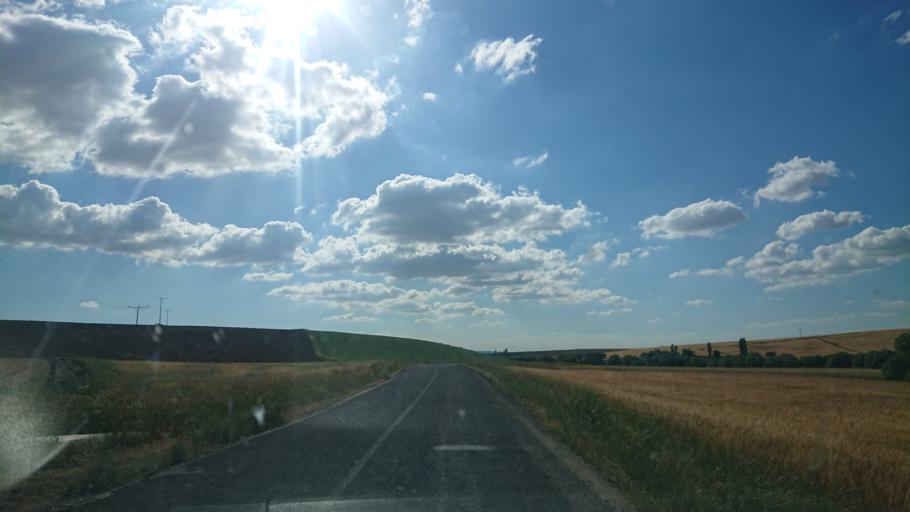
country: TR
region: Aksaray
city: Ortakoy
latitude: 38.7552
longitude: 33.9236
